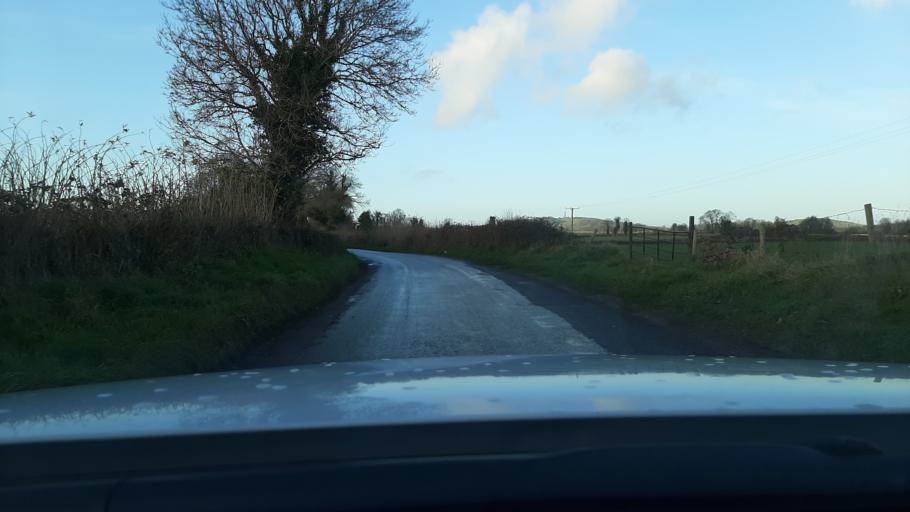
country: IE
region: Leinster
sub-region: Kildare
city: Kildare
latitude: 53.1652
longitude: -6.9213
